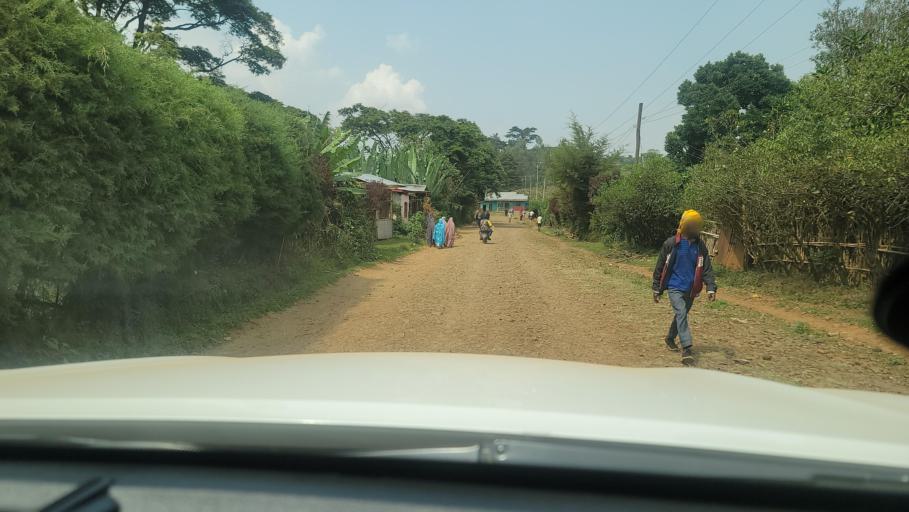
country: ET
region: Oromiya
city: Agaro
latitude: 7.8061
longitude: 36.4666
